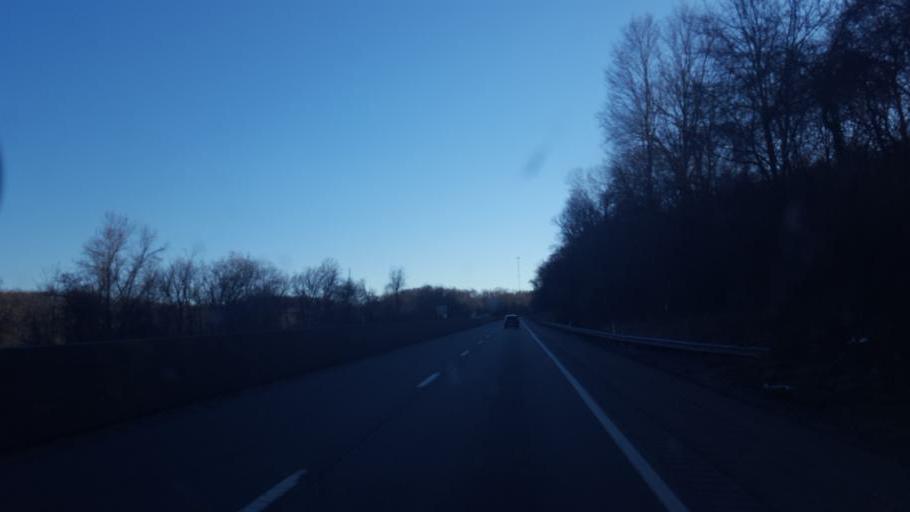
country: US
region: Pennsylvania
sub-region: Westmoreland County
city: New Stanton
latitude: 40.1975
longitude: -79.6844
